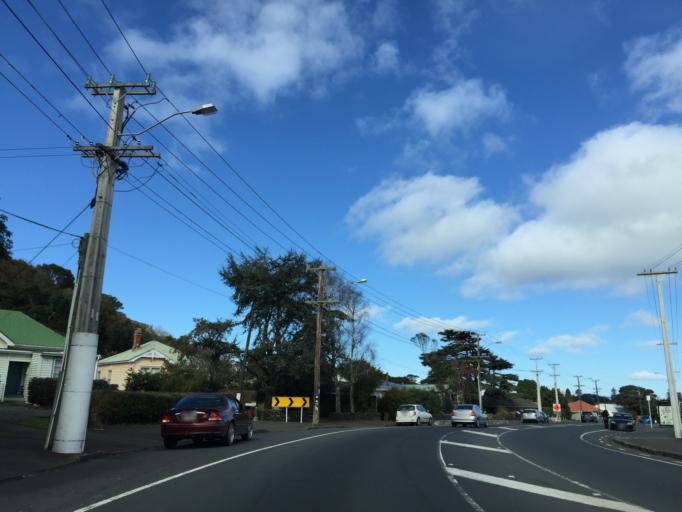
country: NZ
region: Auckland
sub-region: Auckland
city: Auckland
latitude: -36.9017
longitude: 174.7591
